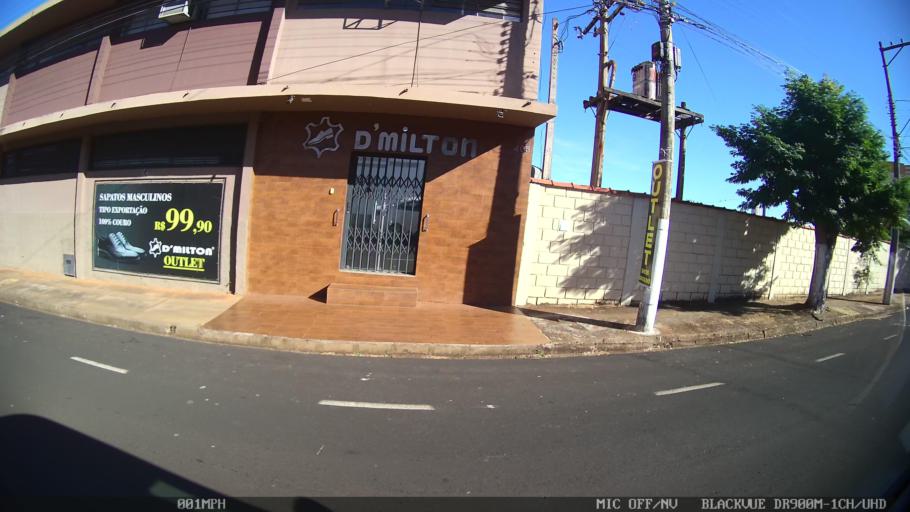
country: BR
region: Sao Paulo
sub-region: Franca
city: Franca
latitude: -20.5493
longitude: -47.4074
